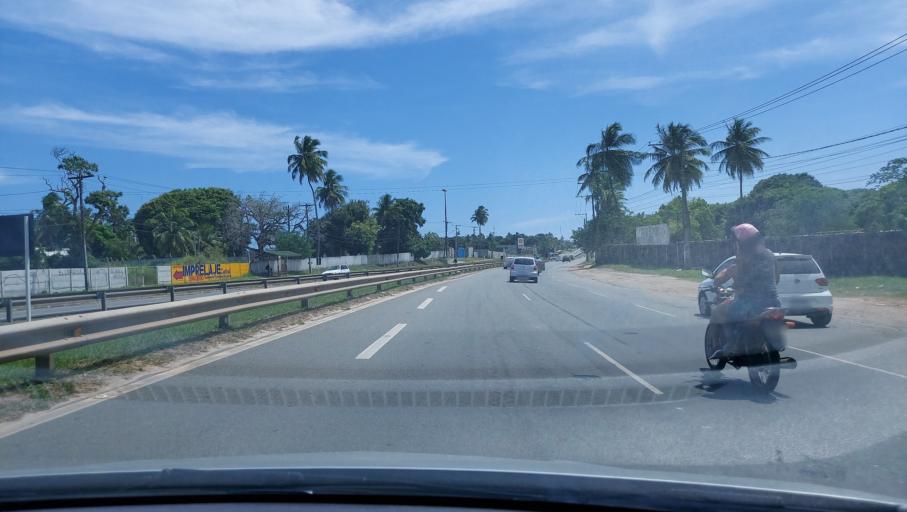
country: BR
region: Bahia
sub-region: Lauro De Freitas
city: Lauro de Freitas
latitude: -12.8448
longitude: -38.2787
